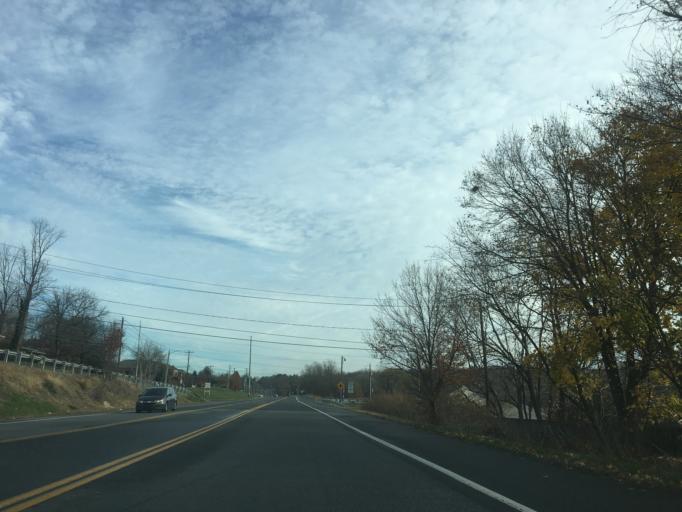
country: US
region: Pennsylvania
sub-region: Perry County
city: Marysville
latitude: 40.3264
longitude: -76.8850
